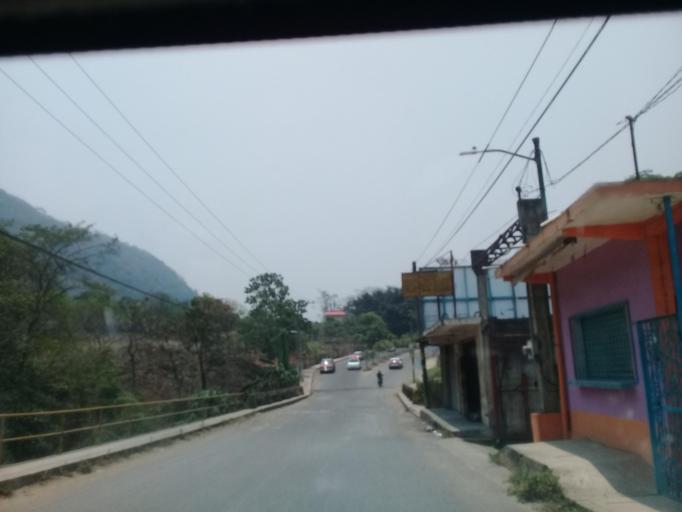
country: MX
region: Veracruz
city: Tezonapa
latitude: 18.6067
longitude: -96.6887
